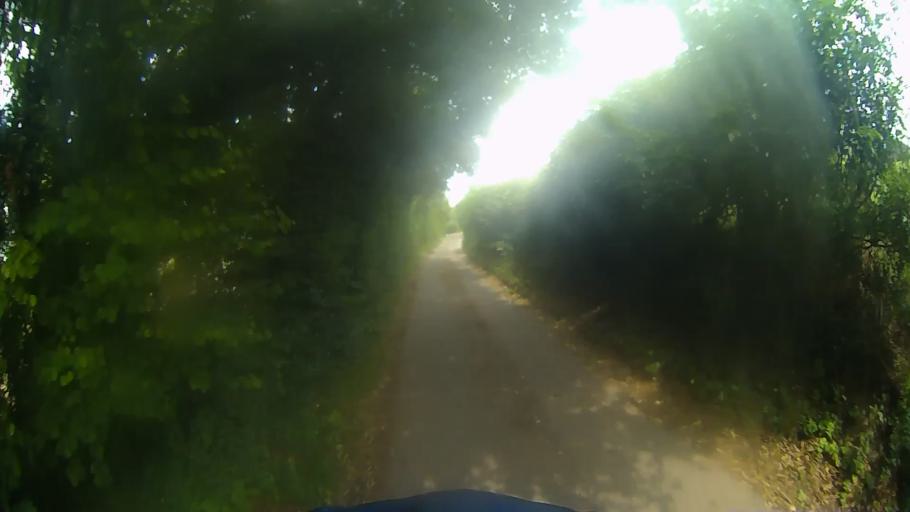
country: GB
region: England
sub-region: Hampshire
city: Overton
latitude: 51.2610
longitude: -1.3237
